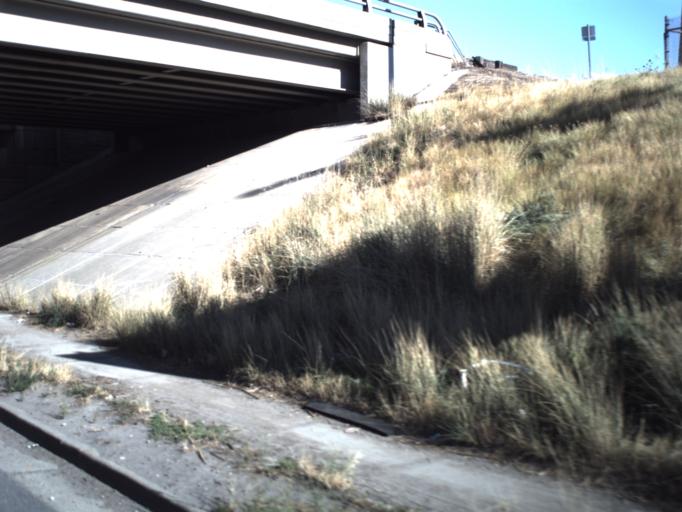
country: US
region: Utah
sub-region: Salt Lake County
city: Centerfield
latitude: 40.6997
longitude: -111.9045
